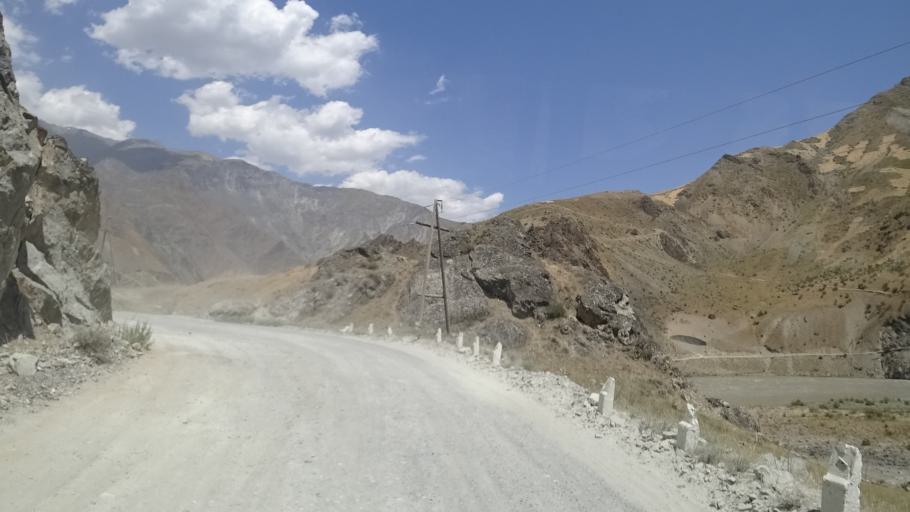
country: AF
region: Badakhshan
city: Nusay
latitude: 38.4520
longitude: 70.8564
